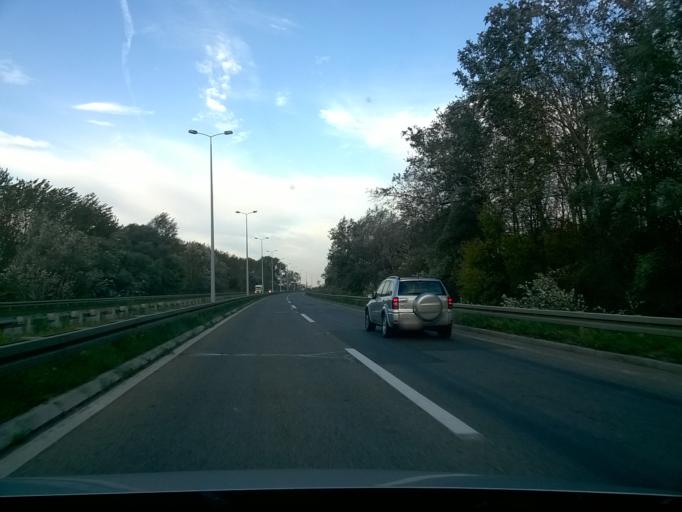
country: RS
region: Autonomna Pokrajina Vojvodina
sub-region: Juznobanatski Okrug
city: Pancevo
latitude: 44.8587
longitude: 20.6003
